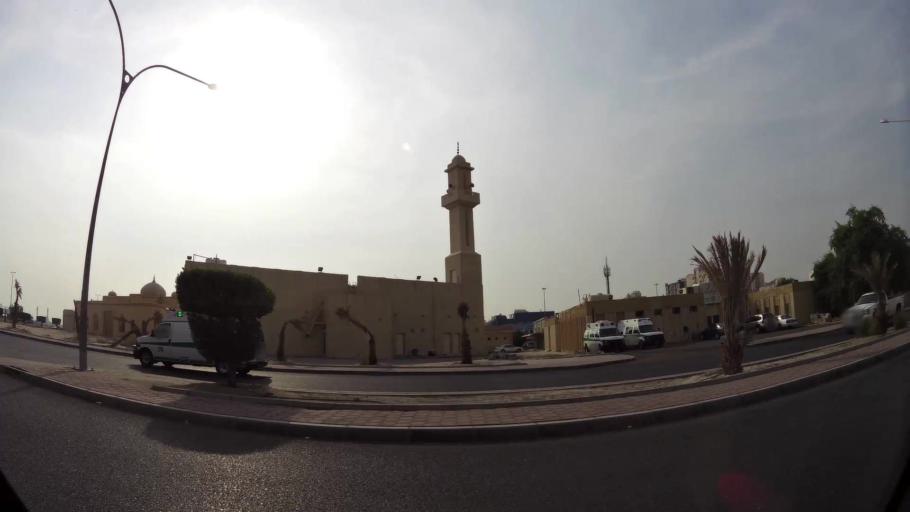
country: KW
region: Al Farwaniyah
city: Janub as Surrah
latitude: 29.2778
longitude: 47.9777
